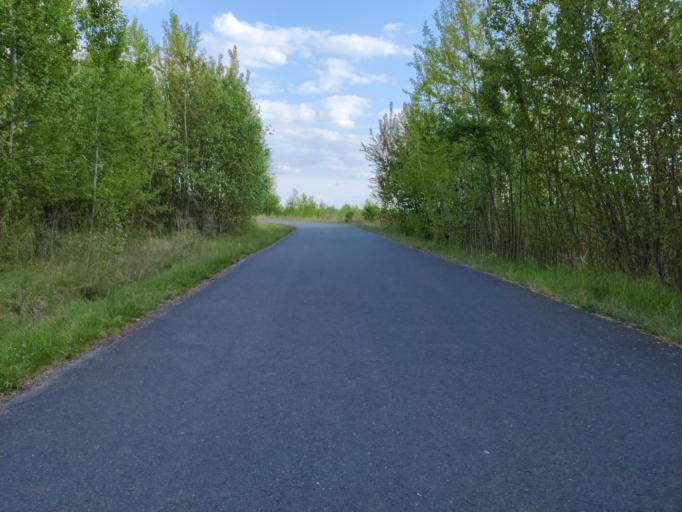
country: DE
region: Saxony
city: Espenhain
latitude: 51.2260
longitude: 12.4545
